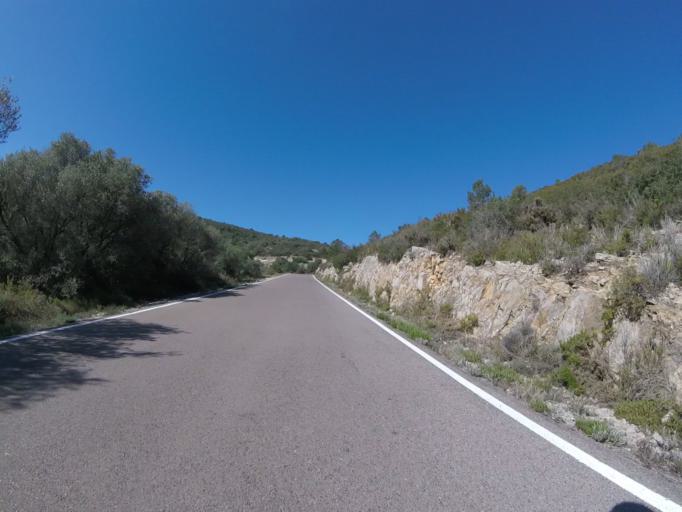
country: ES
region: Valencia
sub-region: Provincia de Castello
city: Santa Magdalena de Pulpis
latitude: 40.3850
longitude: 0.2565
